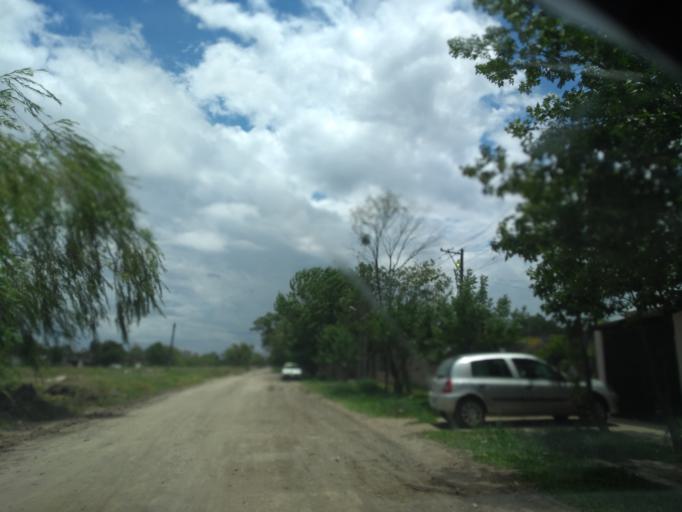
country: AR
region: Chaco
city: Resistencia
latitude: -27.4738
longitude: -58.9695
